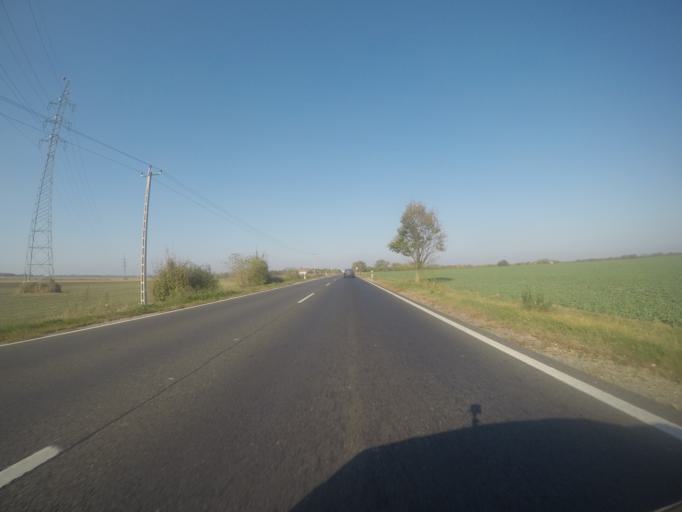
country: HU
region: Fejer
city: Baracs
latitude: 46.8465
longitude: 18.9110
